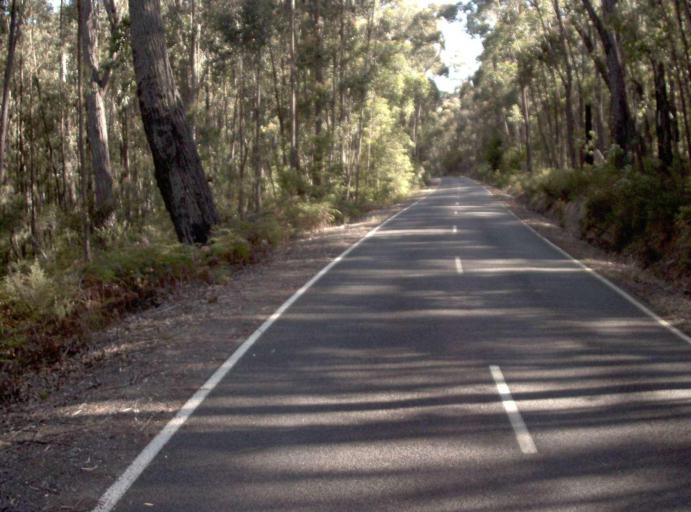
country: AU
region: Victoria
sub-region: East Gippsland
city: Lakes Entrance
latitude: -37.5966
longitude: 148.5279
